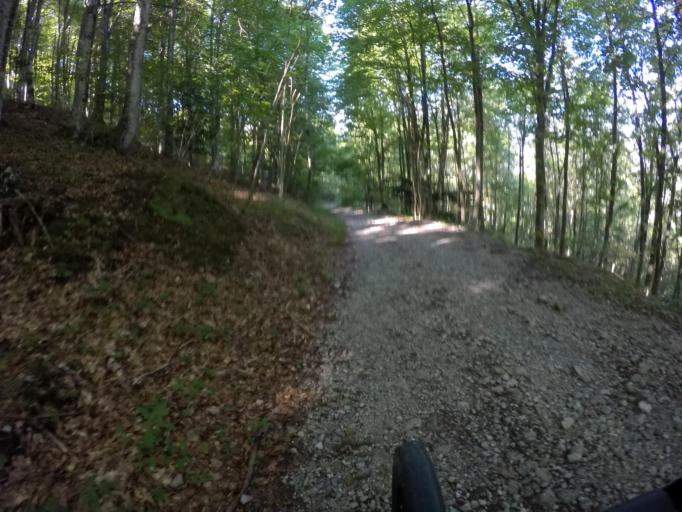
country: IT
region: Friuli Venezia Giulia
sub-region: Provincia di Udine
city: Paularo
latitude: 46.4673
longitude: 13.1053
